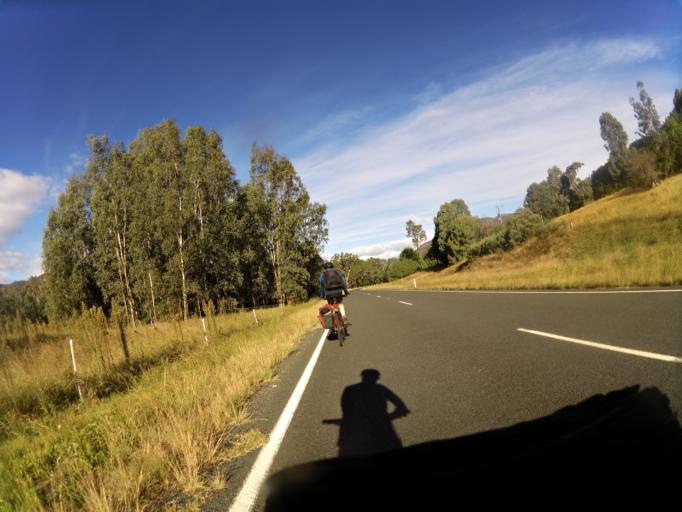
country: AU
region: New South Wales
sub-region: Greater Hume Shire
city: Holbrook
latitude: -35.9732
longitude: 147.8078
